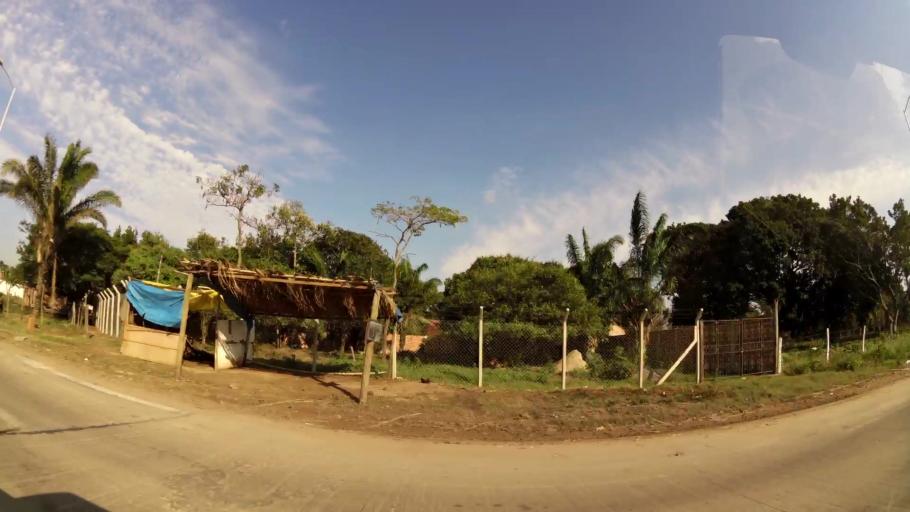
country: BO
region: Santa Cruz
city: Santa Cruz de la Sierra
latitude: -17.7117
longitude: -63.1270
